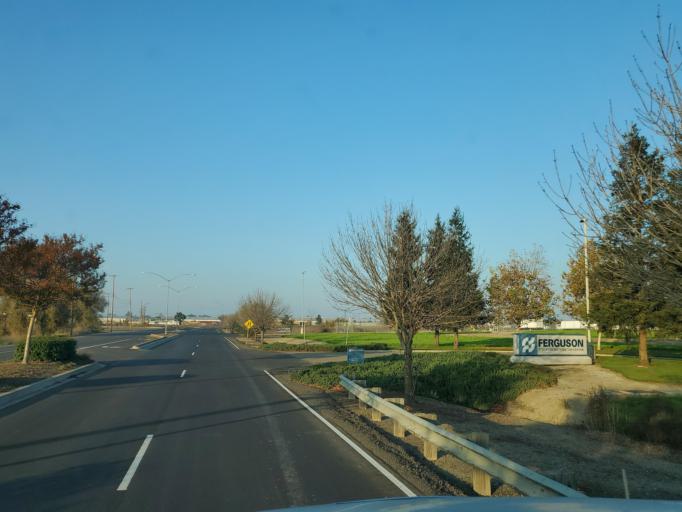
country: US
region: California
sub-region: San Joaquin County
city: Country Club
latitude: 37.9434
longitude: -121.3587
